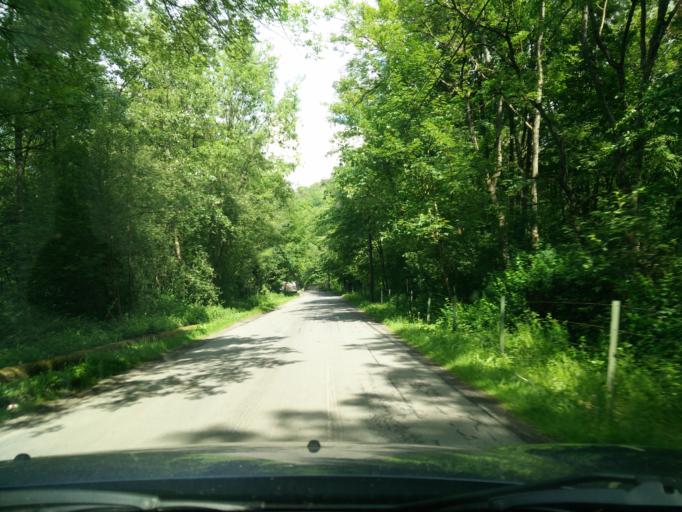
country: BE
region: Wallonia
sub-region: Province de Namur
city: Couvin
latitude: 50.0857
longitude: 4.5623
